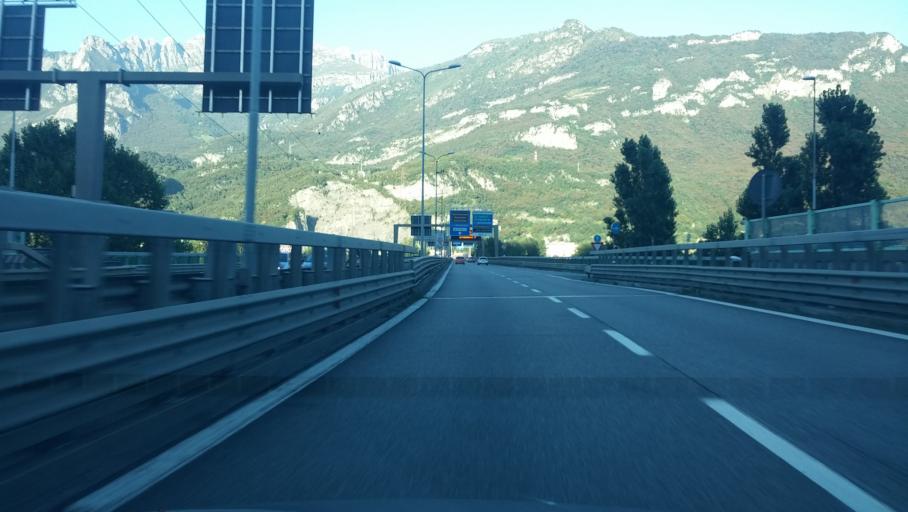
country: IT
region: Lombardy
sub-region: Provincia di Lecco
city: Pescate
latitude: 45.8385
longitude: 9.3968
